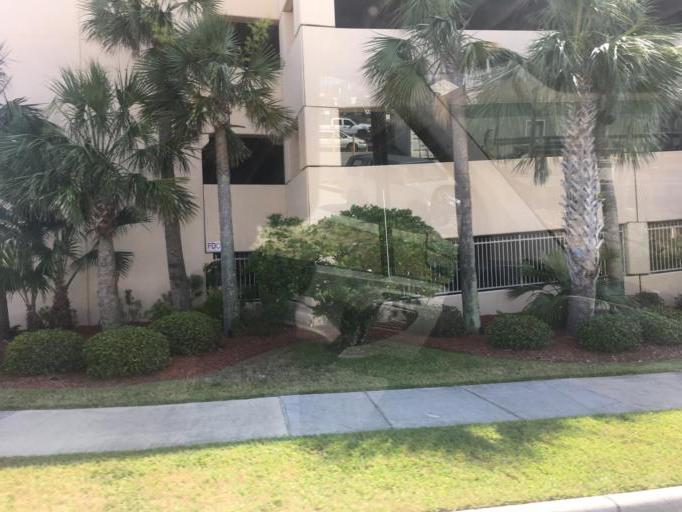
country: US
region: Florida
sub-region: Bay County
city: Panama City Beach
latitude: 30.1670
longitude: -85.7899
